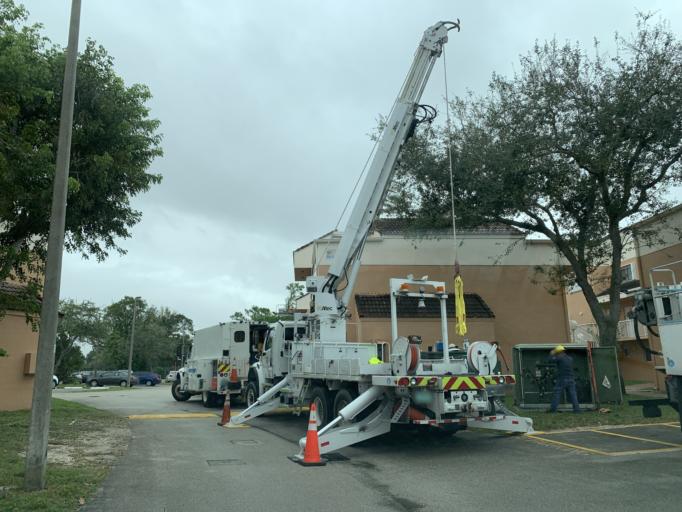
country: US
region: Florida
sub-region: Miami-Dade County
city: Kendall West
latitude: 25.6943
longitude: -80.4337
